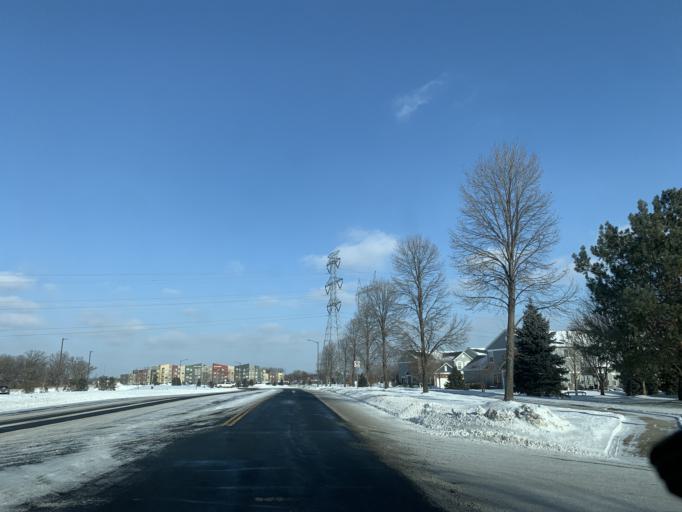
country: US
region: Minnesota
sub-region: Scott County
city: Prior Lake
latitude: 44.7760
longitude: -93.4098
